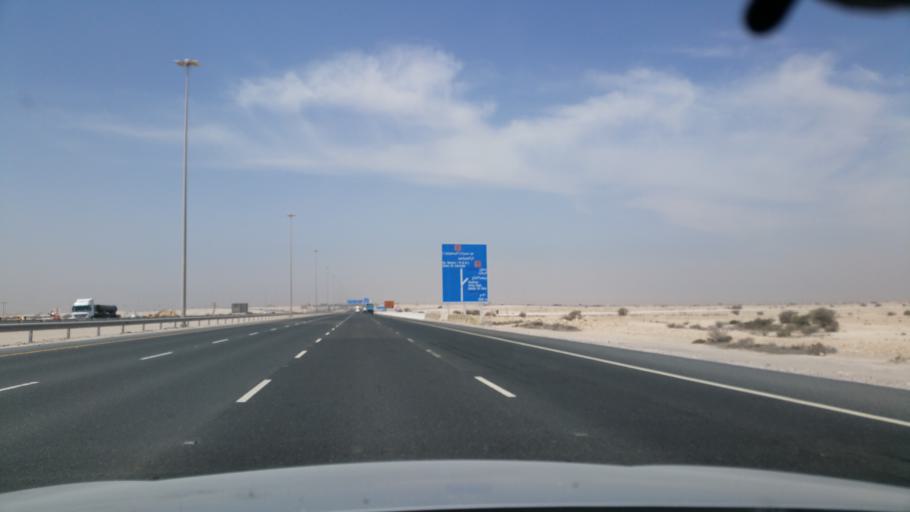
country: QA
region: Baladiyat ar Rayyan
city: Ash Shahaniyah
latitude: 25.1153
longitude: 51.1786
